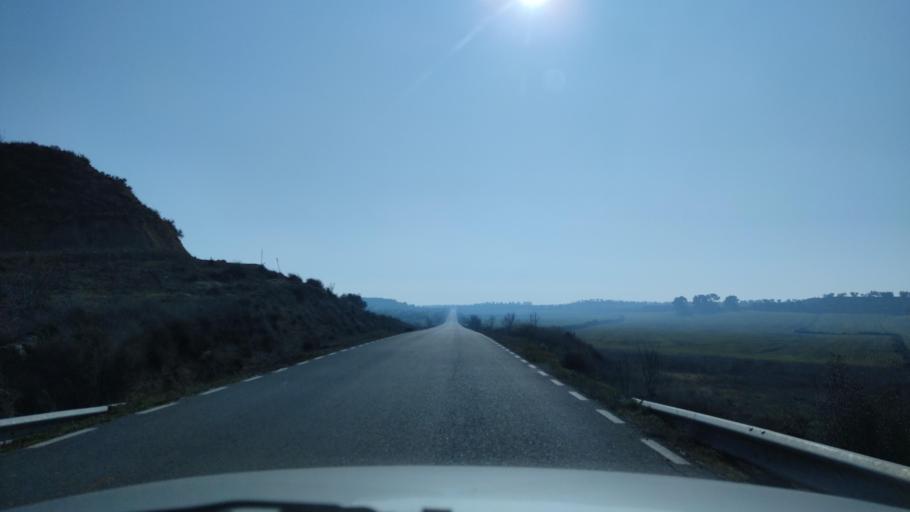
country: ES
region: Catalonia
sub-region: Provincia de Lleida
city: Alcano
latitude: 41.4765
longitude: 0.5604
